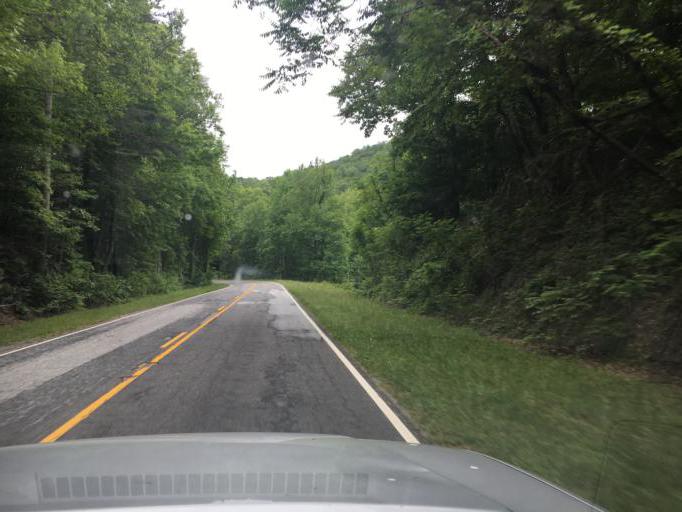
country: US
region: South Carolina
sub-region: Greenville County
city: Tigerville
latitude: 35.1429
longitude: -82.4224
